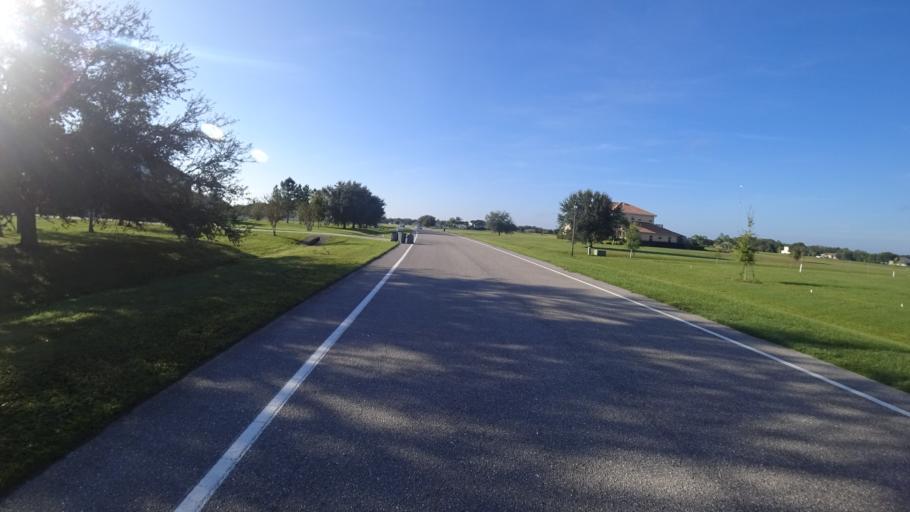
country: US
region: Florida
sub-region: Hillsborough County
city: Sun City Center
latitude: 27.5668
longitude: -82.3533
